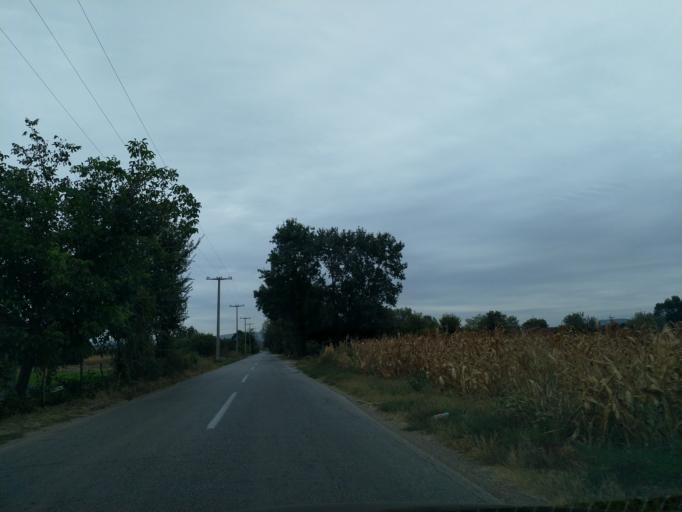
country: RS
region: Central Serbia
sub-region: Pomoravski Okrug
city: Paracin
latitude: 43.8484
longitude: 21.3838
